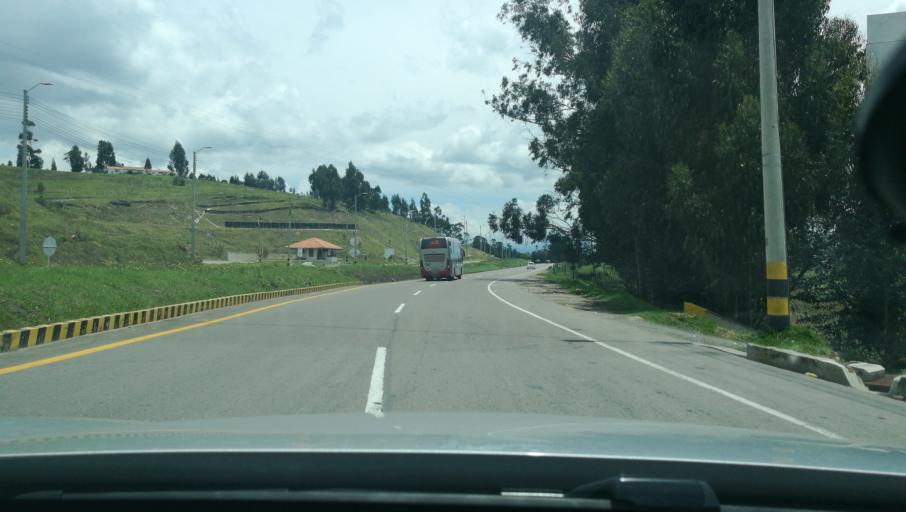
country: CO
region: Boyaca
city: Combita
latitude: 5.6577
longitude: -73.2774
